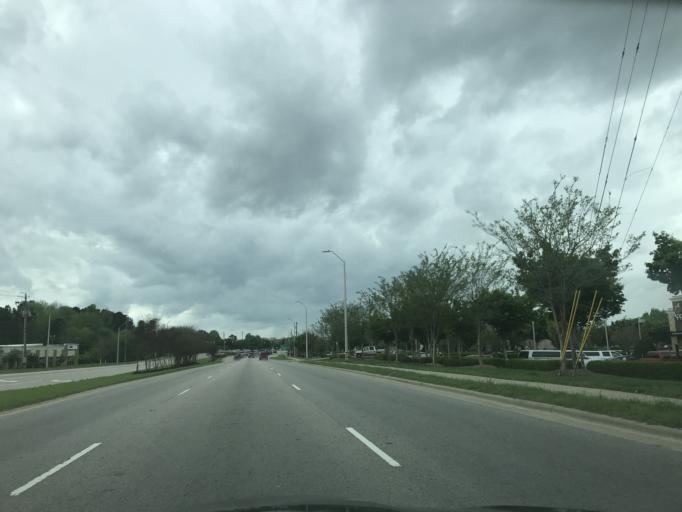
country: US
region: North Carolina
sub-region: Wake County
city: Knightdale
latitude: 35.7967
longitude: -78.5068
